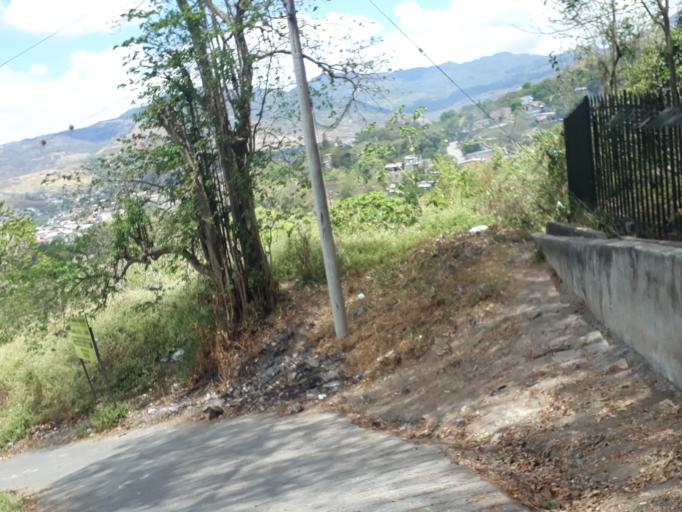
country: NI
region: Matagalpa
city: Matagalpa
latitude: 12.9195
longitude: -85.9129
